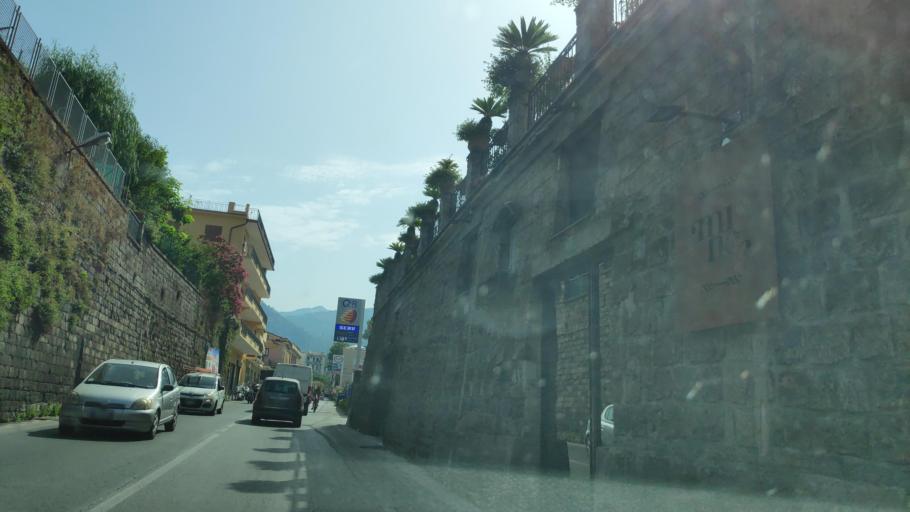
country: IT
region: Campania
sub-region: Provincia di Napoli
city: Sant'Agnello
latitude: 40.6304
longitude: 14.4028
